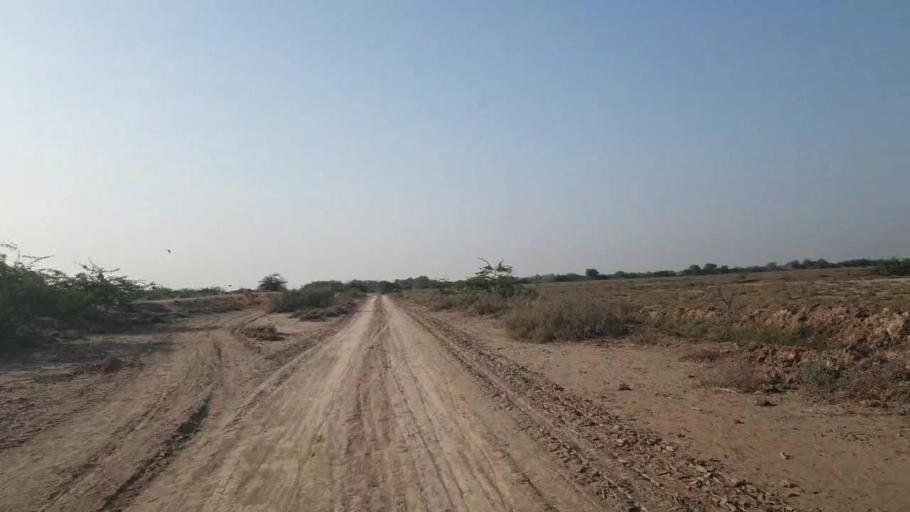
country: PK
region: Sindh
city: Badin
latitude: 24.4624
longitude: 68.7369
